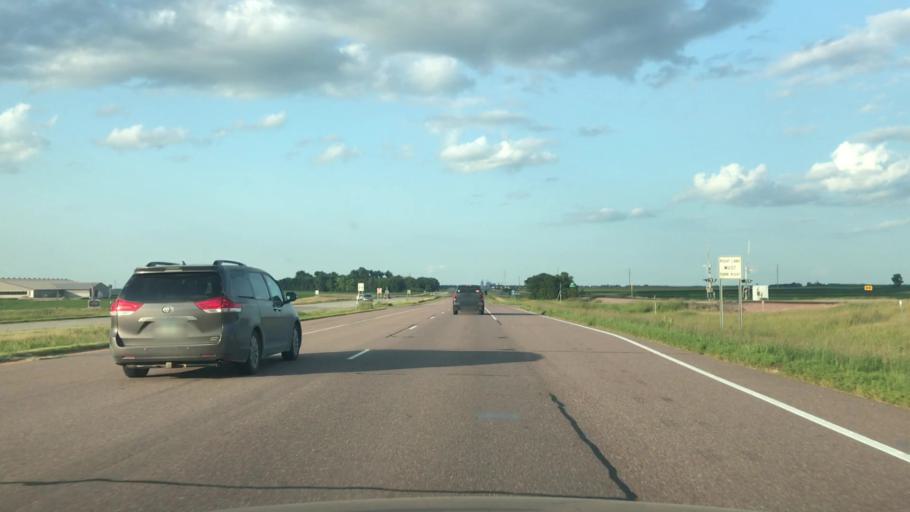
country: US
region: Minnesota
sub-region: Nobles County
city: Worthington
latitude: 43.6597
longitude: -95.5313
